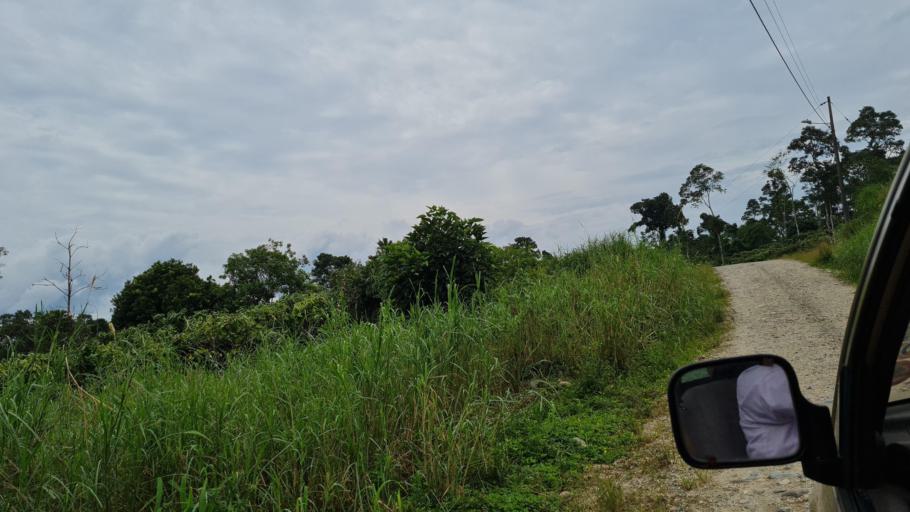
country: EC
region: Napo
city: Tena
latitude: -0.9938
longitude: -77.7520
